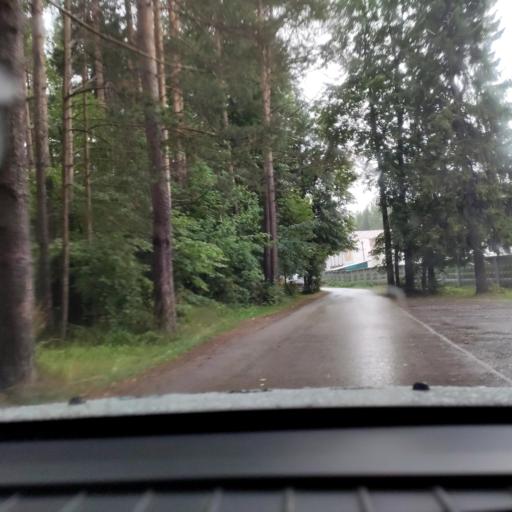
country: RU
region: Perm
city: Perm
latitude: 58.1021
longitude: 56.2797
